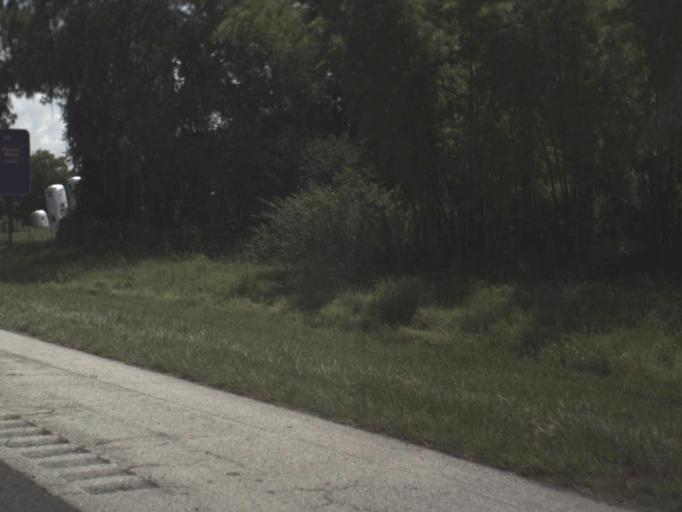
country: US
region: Florida
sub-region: Hillsborough County
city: Dover
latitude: 28.0211
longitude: -82.2532
